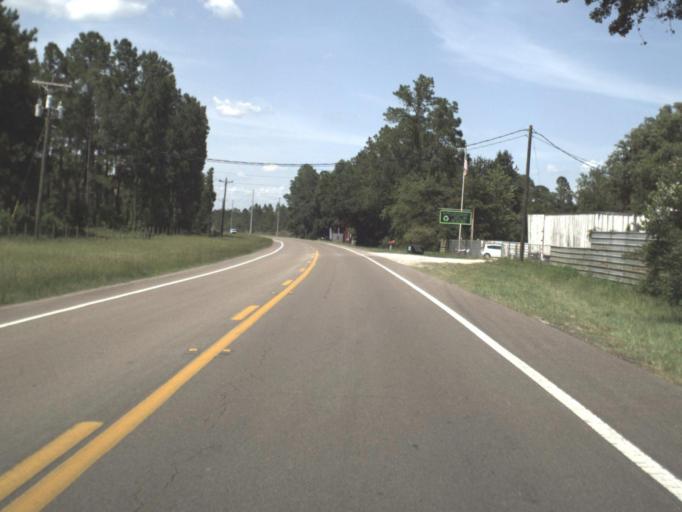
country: US
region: Florida
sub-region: Gilchrist County
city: Trenton
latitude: 29.6368
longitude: -82.7969
